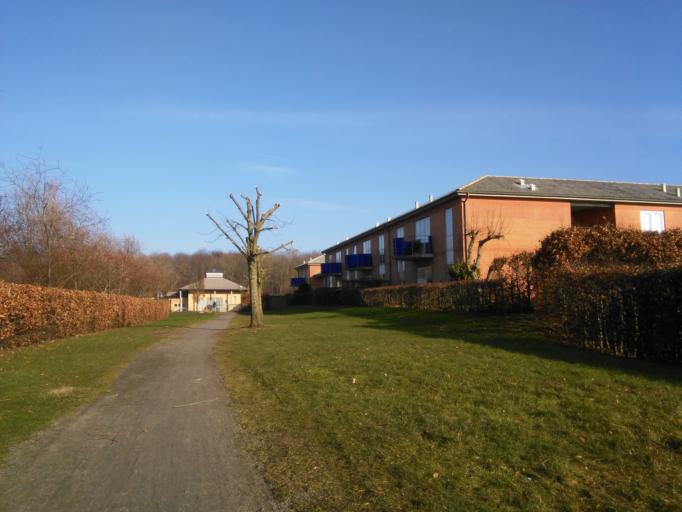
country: DK
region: Central Jutland
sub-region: Arhus Kommune
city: Malling
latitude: 56.0421
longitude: 10.2049
